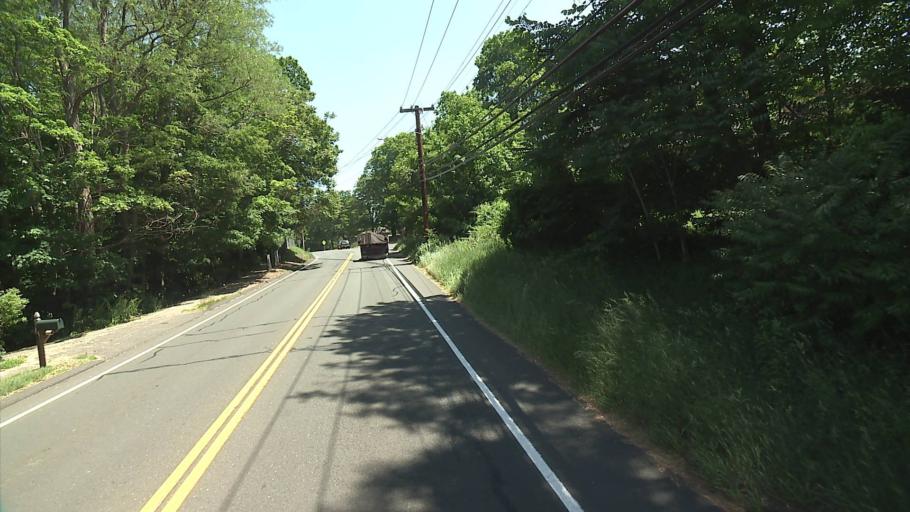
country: US
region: Connecticut
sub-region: Tolland County
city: Rockville
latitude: 41.8365
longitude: -72.4679
